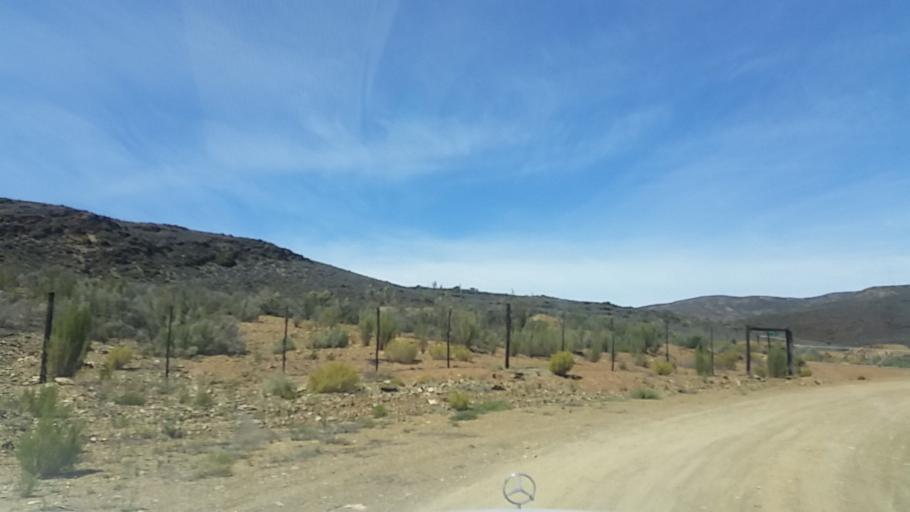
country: ZA
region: Western Cape
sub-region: Eden District Municipality
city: Knysna
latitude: -33.6483
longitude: 23.1381
